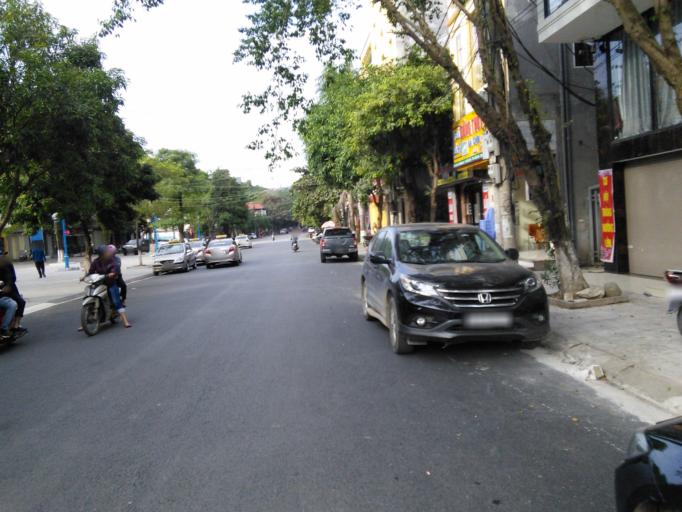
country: VN
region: Lao Cai
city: Lao Cai
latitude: 22.4940
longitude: 103.9691
